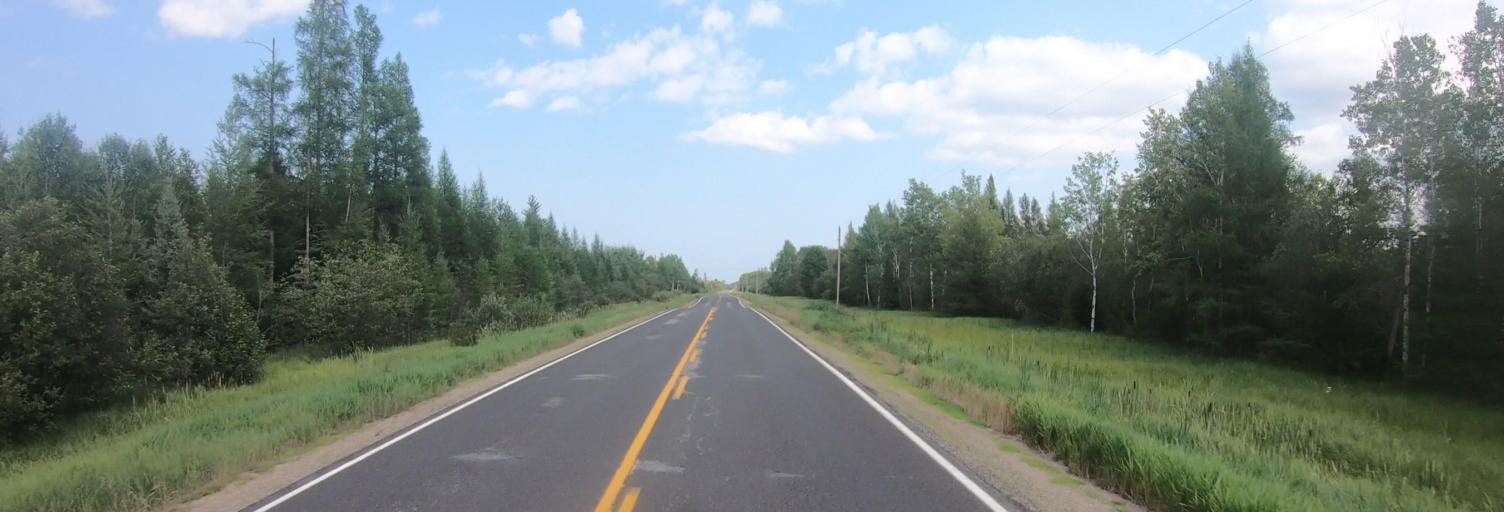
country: US
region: Minnesota
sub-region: Saint Louis County
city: Mountain Iron
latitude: 47.8917
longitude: -92.6847
